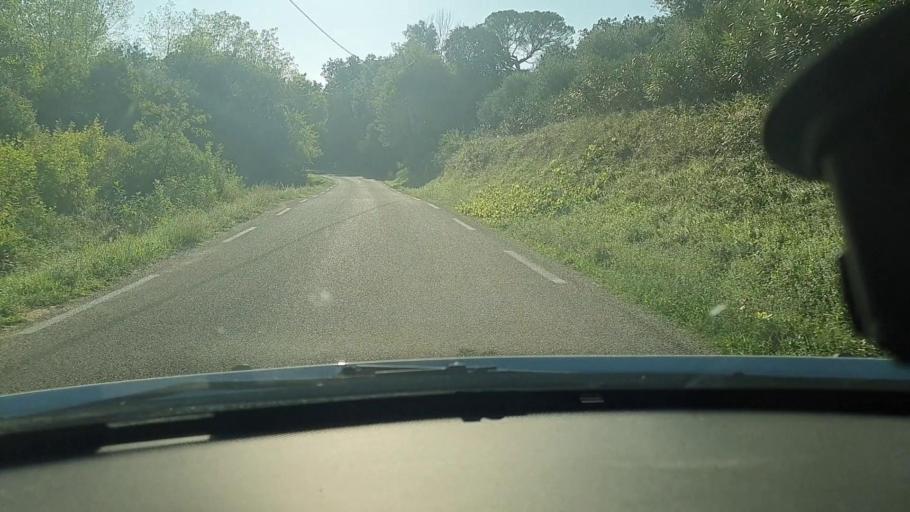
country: FR
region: Languedoc-Roussillon
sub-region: Departement du Gard
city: Goudargues
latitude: 44.2321
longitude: 4.4430
